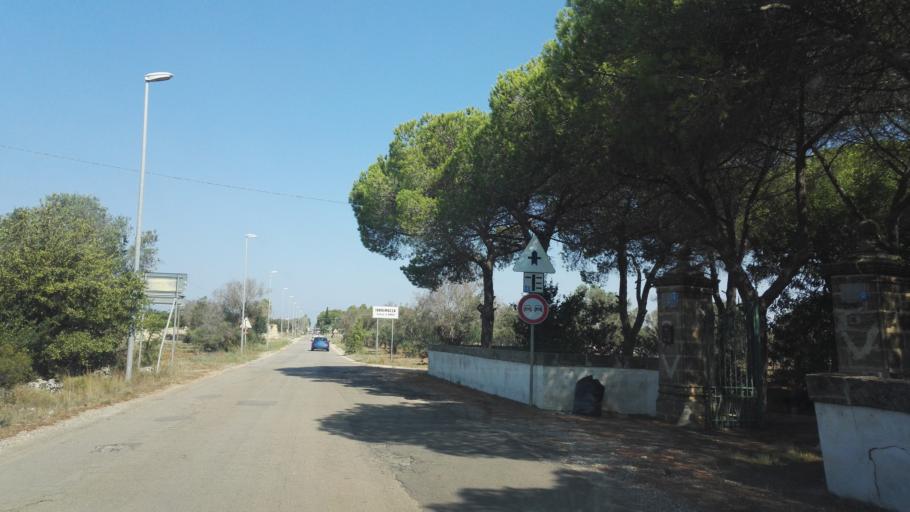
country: IT
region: Apulia
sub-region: Provincia di Lecce
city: Nardo
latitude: 40.1403
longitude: 18.0139
